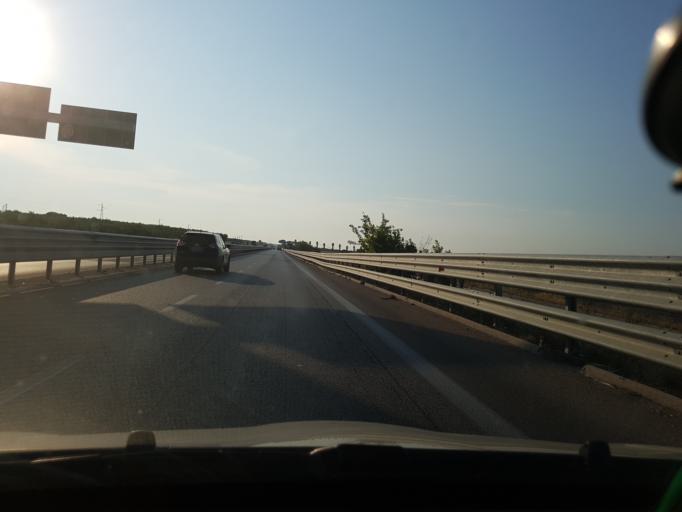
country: IT
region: Apulia
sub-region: Provincia di Foggia
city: Stornara
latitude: 41.3110
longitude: 15.8009
